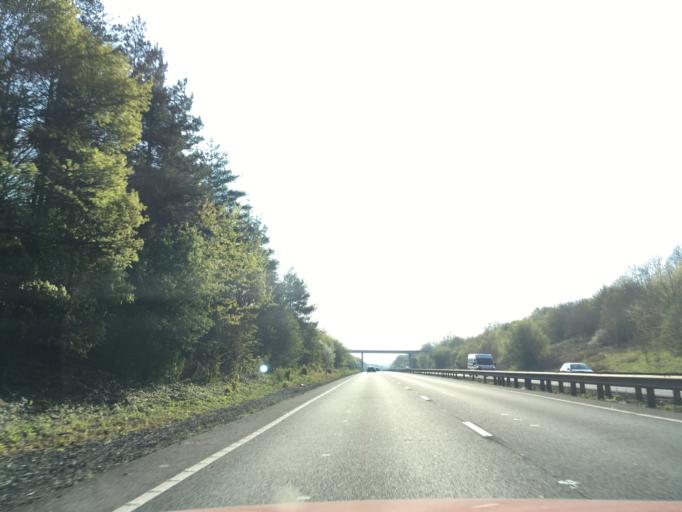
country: GB
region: England
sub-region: Milton Keynes
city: Calverton
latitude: 52.0503
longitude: -0.8221
